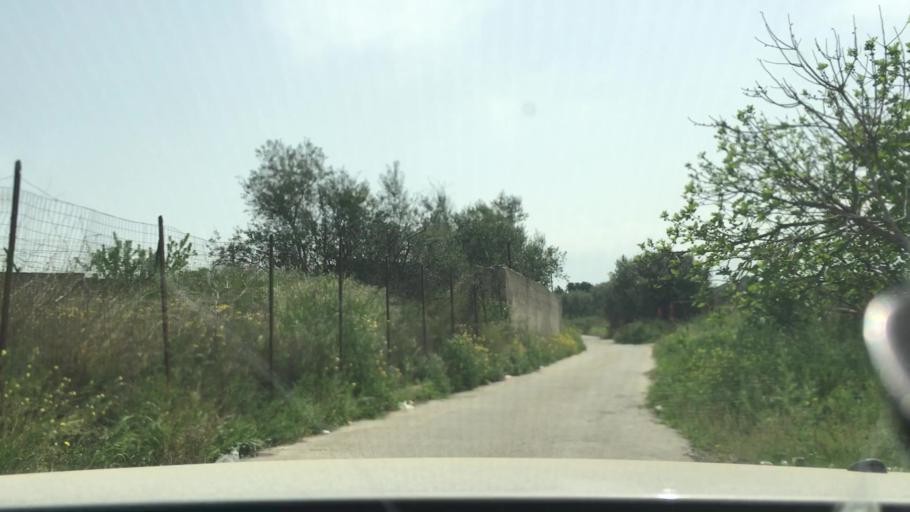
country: IT
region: Apulia
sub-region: Provincia di Barletta - Andria - Trani
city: Capirro
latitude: 41.2579
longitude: 16.4531
